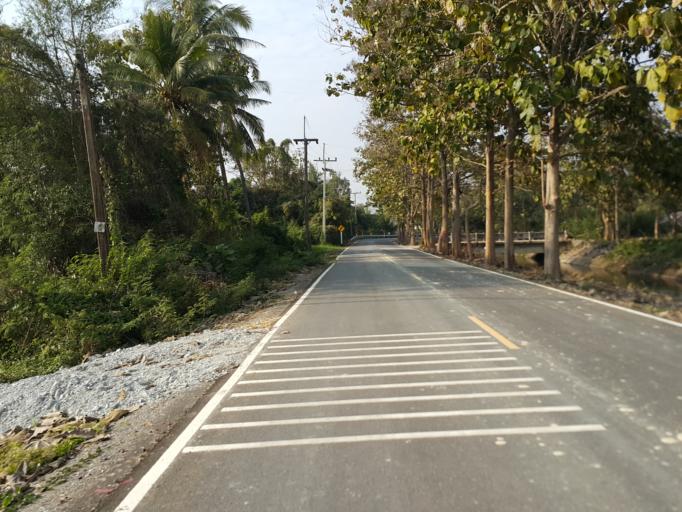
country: TH
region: Chiang Mai
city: San Sai
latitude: 18.8760
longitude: 99.1448
